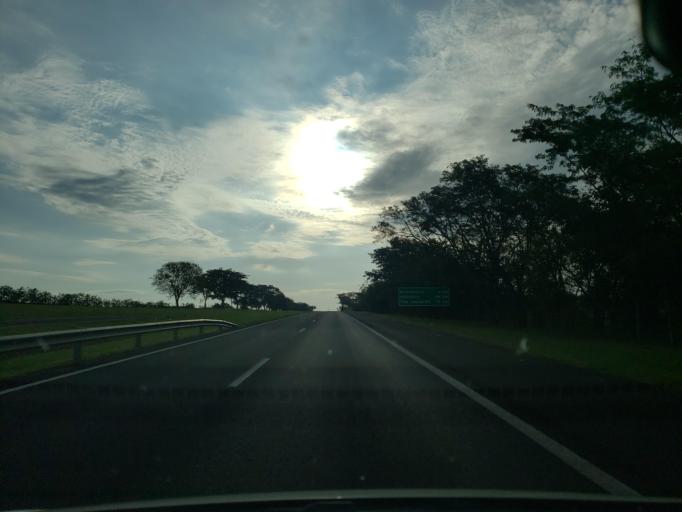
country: BR
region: Sao Paulo
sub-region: Mirandopolis
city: Mirandopolis
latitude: -21.1143
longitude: -51.0182
